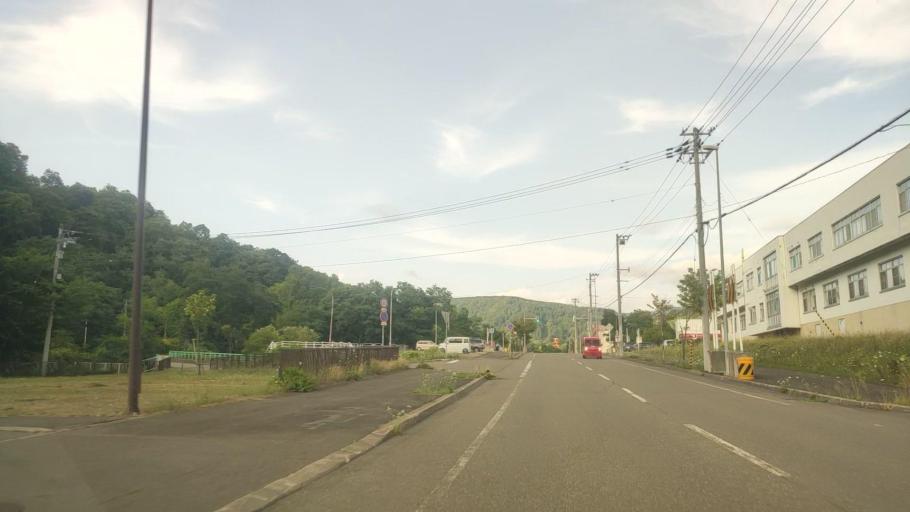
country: JP
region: Hokkaido
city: Iwamizawa
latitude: 43.0609
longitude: 141.9785
